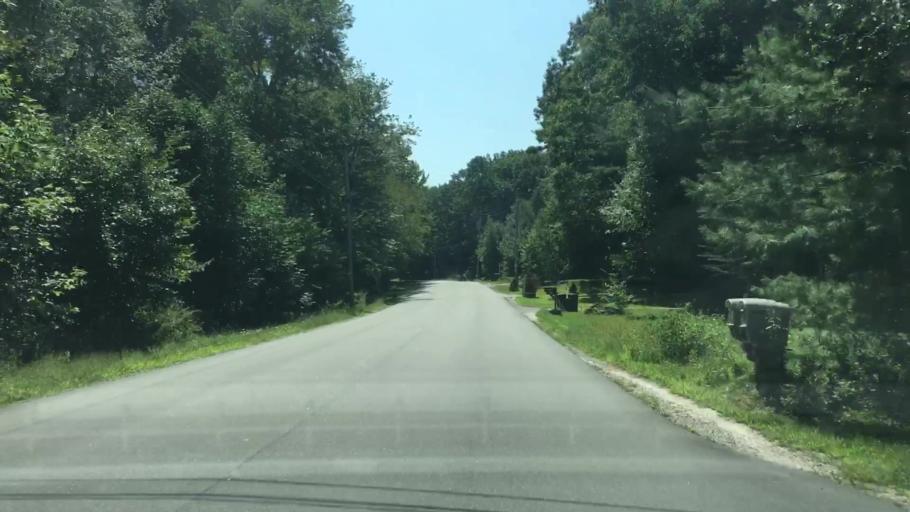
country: US
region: New Hampshire
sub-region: Rockingham County
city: Hampstead
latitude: 42.8904
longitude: -71.2176
